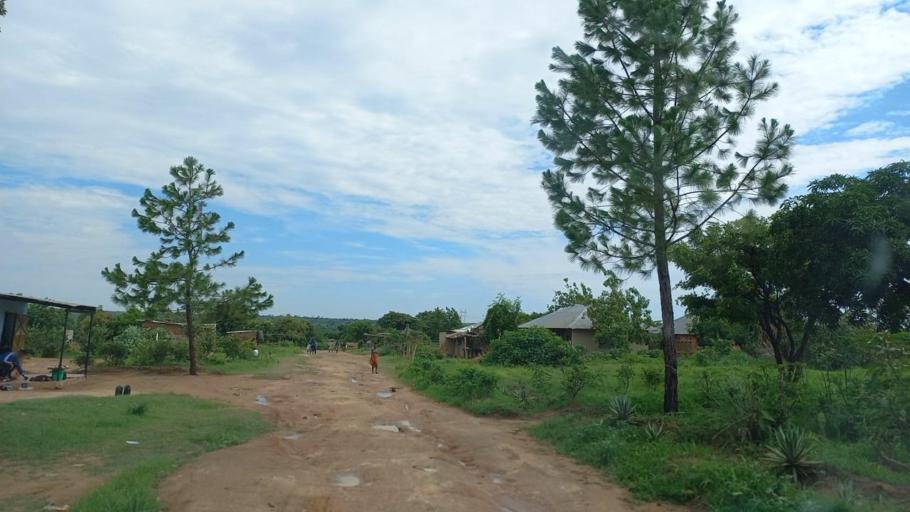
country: ZM
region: Copperbelt
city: Kitwe
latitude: -12.8683
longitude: 28.3347
